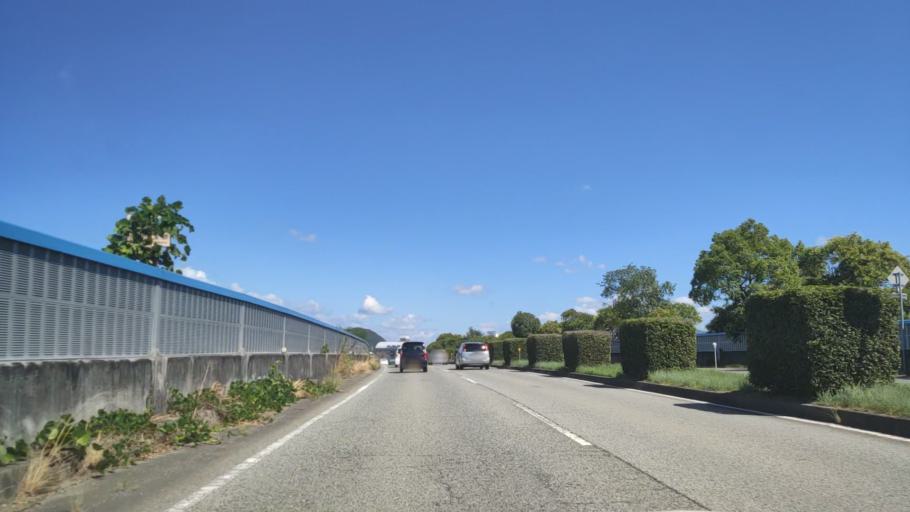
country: JP
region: Hyogo
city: Yashiro
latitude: 34.9231
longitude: 134.9598
